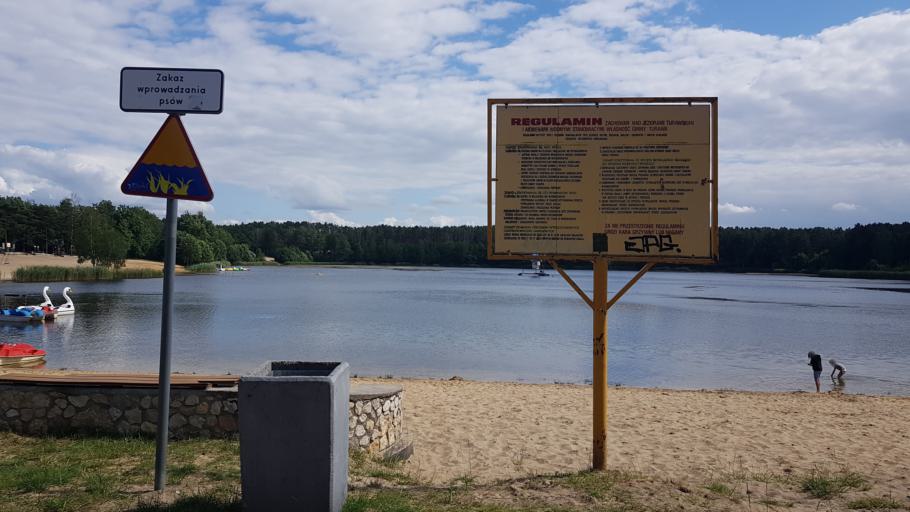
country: PL
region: Opole Voivodeship
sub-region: Powiat opolski
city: Chrzastowice
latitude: 50.7123
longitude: 18.1021
